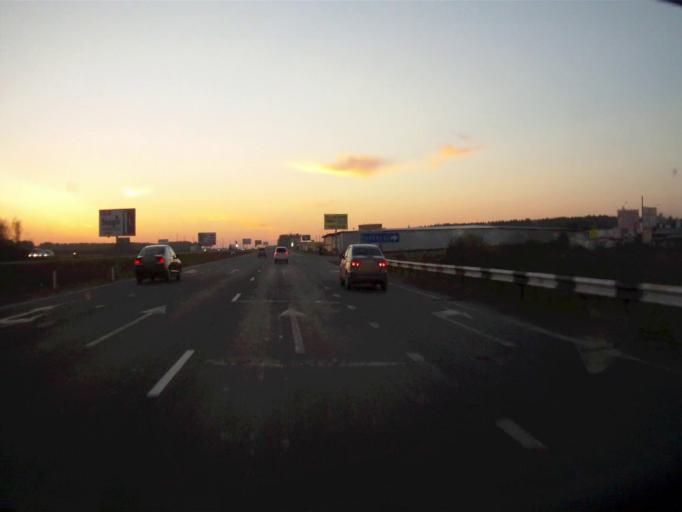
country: RU
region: Chelyabinsk
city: Roshchino
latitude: 55.1845
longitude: 61.2439
